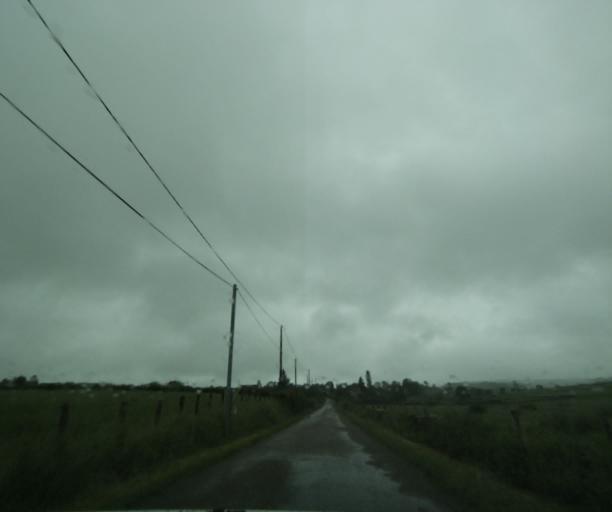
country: FR
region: Bourgogne
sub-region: Departement de Saone-et-Loire
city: Charolles
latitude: 46.3669
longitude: 4.2383
